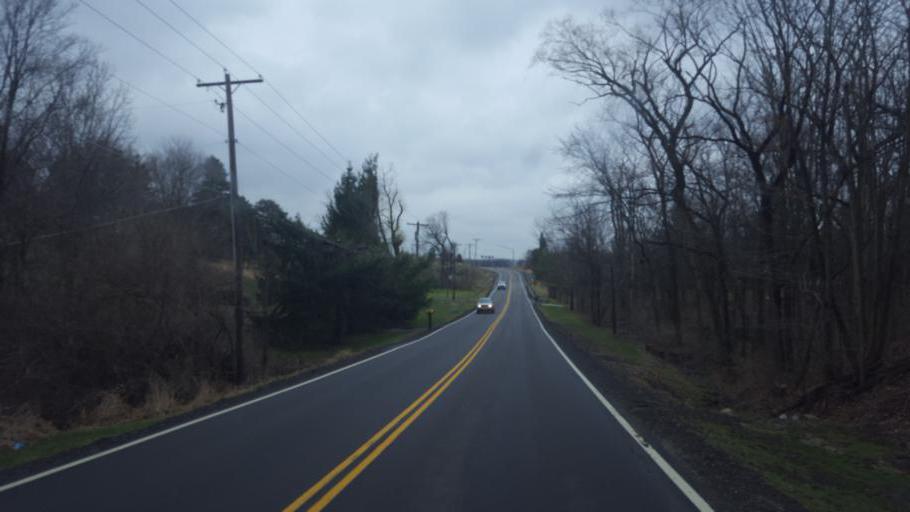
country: US
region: Ohio
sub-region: Medina County
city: Medina
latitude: 41.1066
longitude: -81.8416
